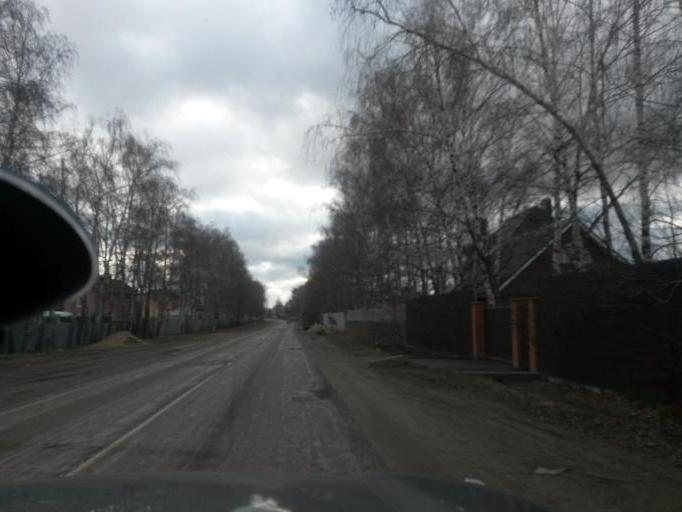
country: RU
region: Moskovskaya
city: Alekseyevka
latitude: 55.6027
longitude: 37.8083
